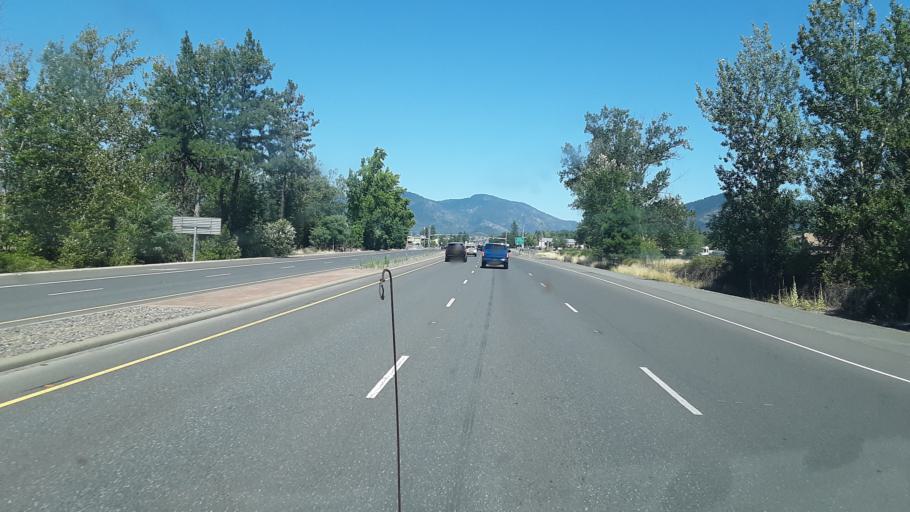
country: US
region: Oregon
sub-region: Josephine County
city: Redwood
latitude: 42.4177
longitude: -123.3714
